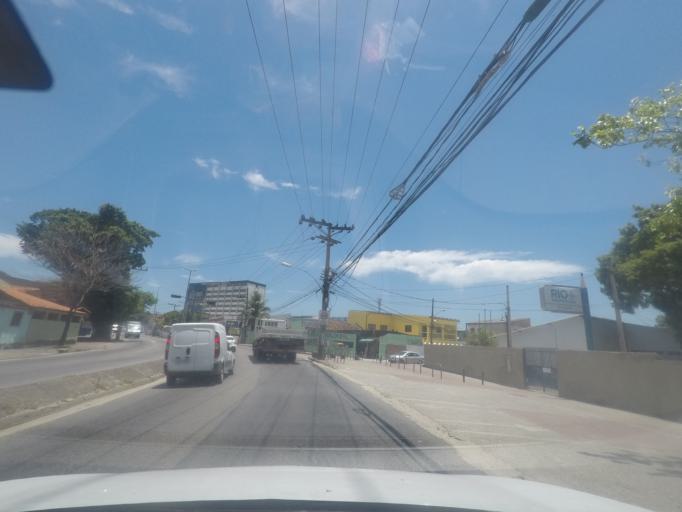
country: BR
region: Rio de Janeiro
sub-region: Itaguai
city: Itaguai
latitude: -22.9103
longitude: -43.6873
